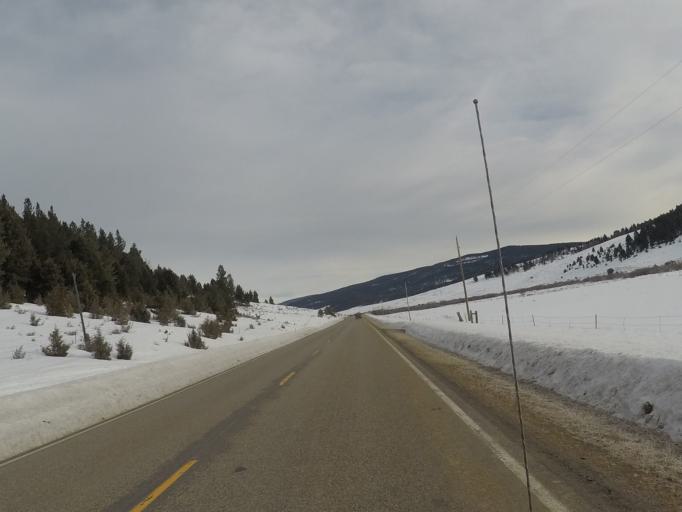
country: US
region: Montana
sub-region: Meagher County
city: White Sulphur Springs
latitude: 46.7098
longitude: -110.8610
